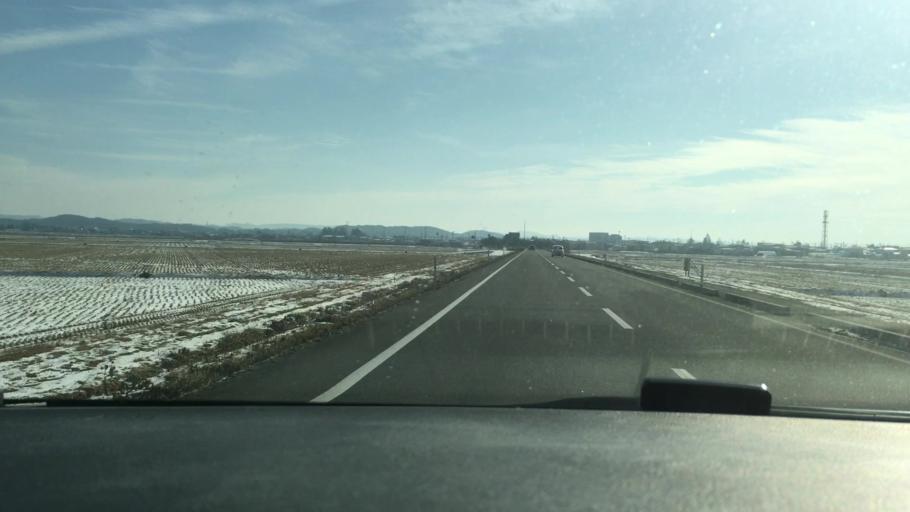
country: JP
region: Iwate
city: Ichinoseki
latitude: 38.7806
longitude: 141.1255
